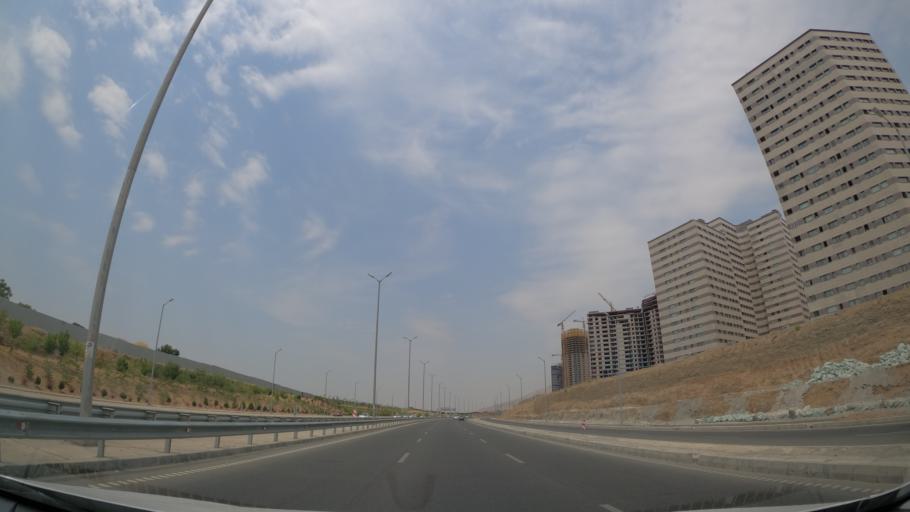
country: IR
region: Tehran
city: Shahr-e Qods
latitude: 35.7463
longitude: 51.1855
